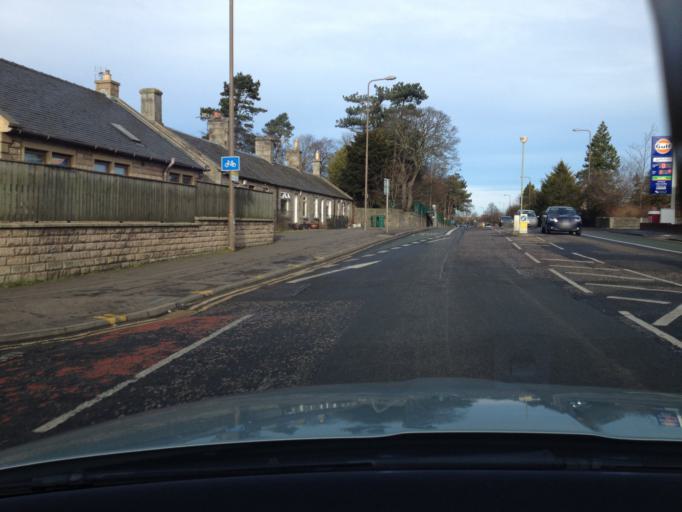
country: GB
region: Scotland
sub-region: Midlothian
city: Loanhead
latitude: 55.9051
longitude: -3.1659
